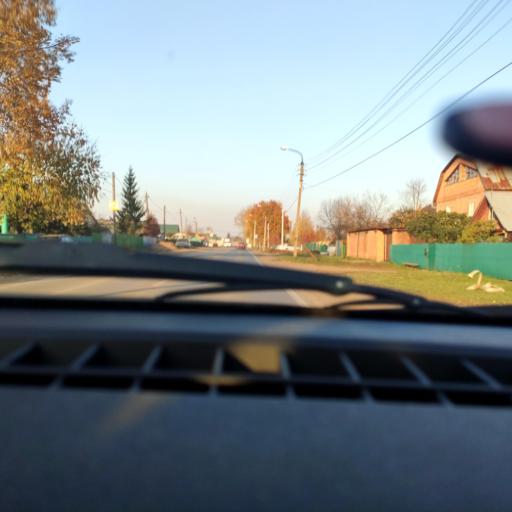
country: RU
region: Bashkortostan
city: Ufa
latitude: 54.8178
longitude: 56.1689
